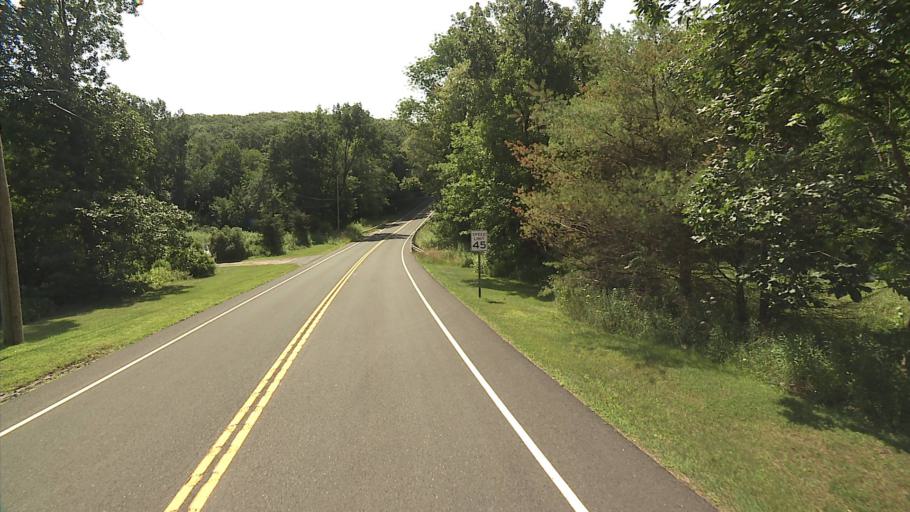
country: US
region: Massachusetts
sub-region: Berkshire County
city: New Marlborough
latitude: 42.0399
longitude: -73.2146
